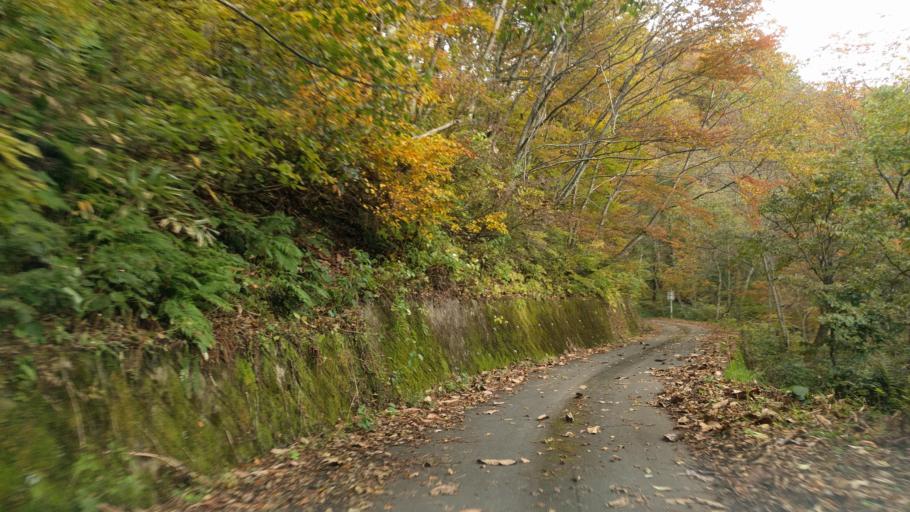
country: JP
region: Fukushima
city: Kitakata
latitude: 37.3901
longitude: 139.7147
